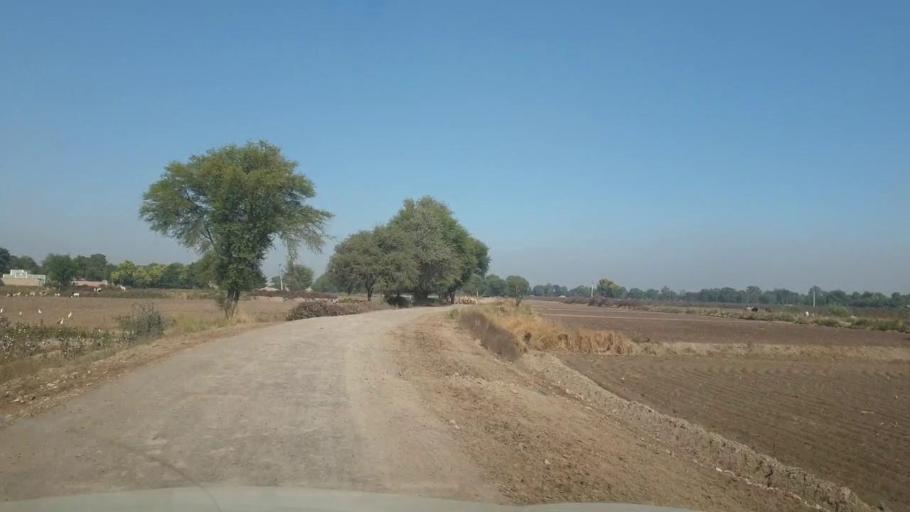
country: PK
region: Sindh
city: Bhan
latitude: 26.5815
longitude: 67.6999
